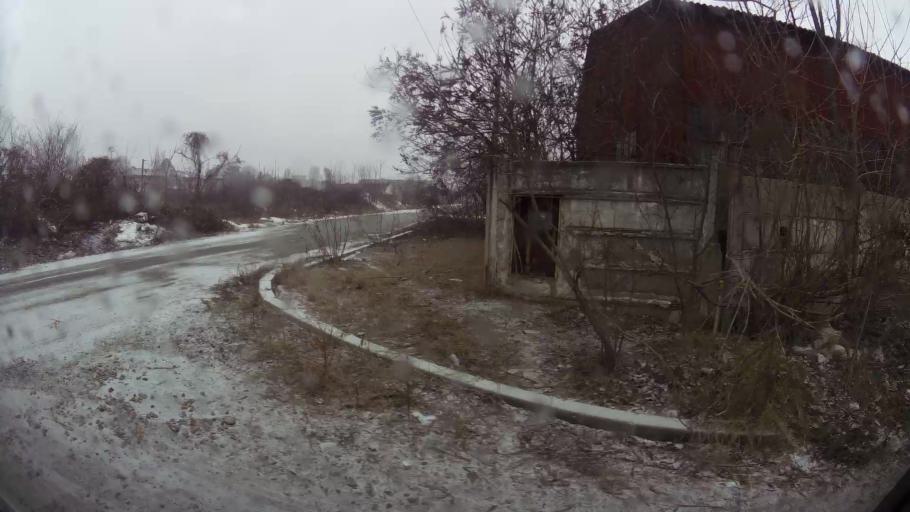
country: RO
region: Prahova
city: Ploiesti
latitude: 44.9537
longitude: 26.0293
